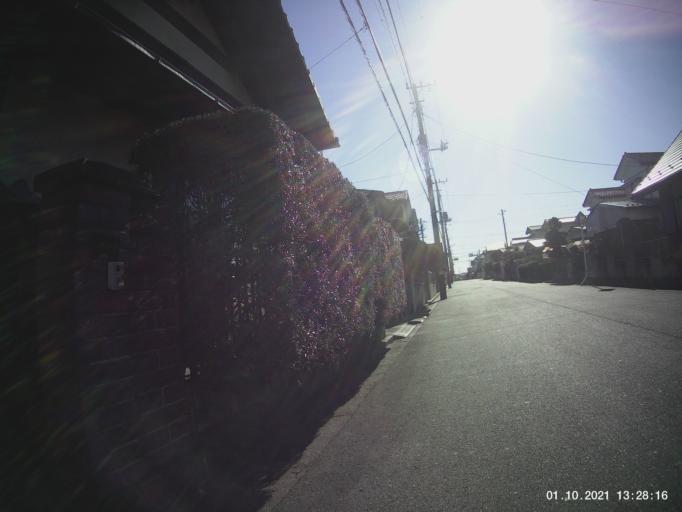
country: JP
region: Chiba
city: Yotsukaido
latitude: 35.5988
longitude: 140.2138
